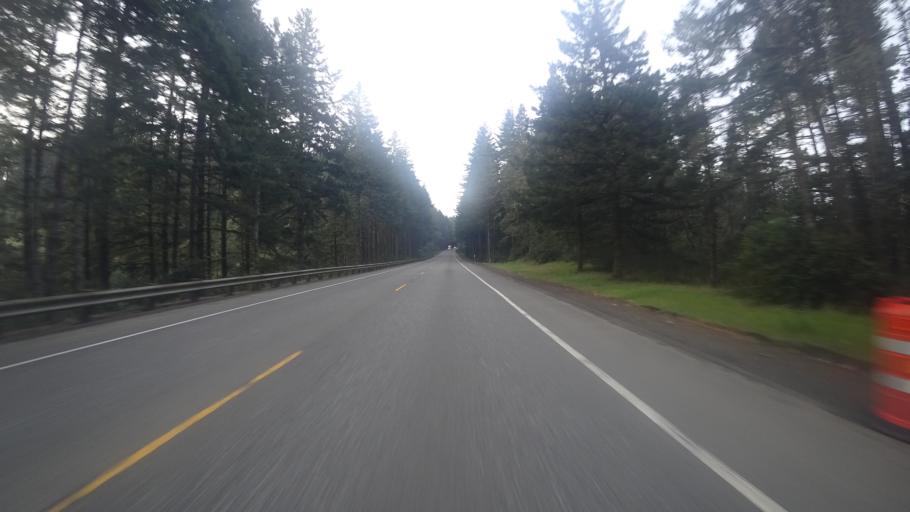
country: US
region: Oregon
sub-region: Coos County
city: Lakeside
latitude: 43.6264
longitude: -124.1828
